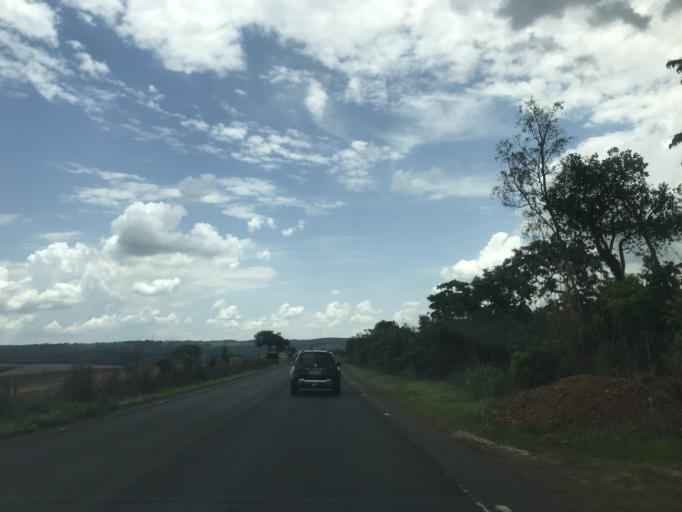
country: BR
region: Goias
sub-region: Vianopolis
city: Vianopolis
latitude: -16.9455
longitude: -48.5640
